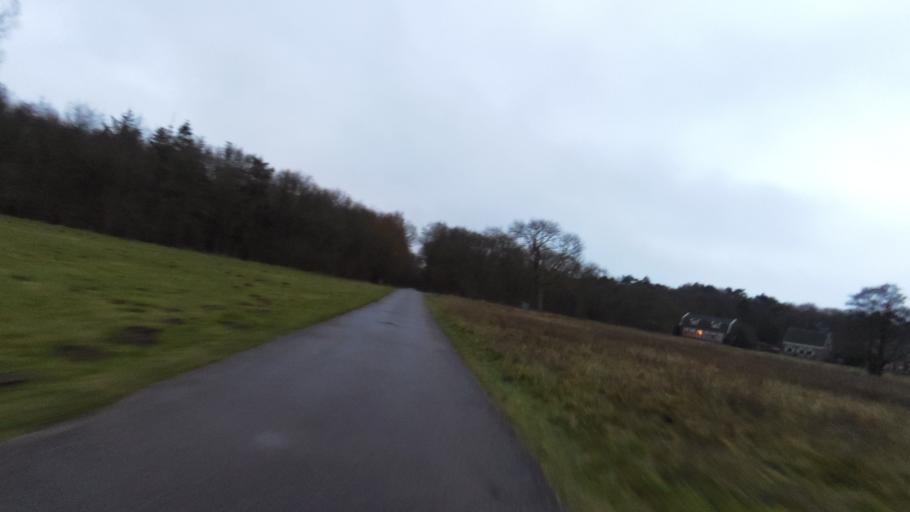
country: NL
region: North Holland
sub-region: Gemeente Heemskerk
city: Heemskerk
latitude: 52.5238
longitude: 4.6312
